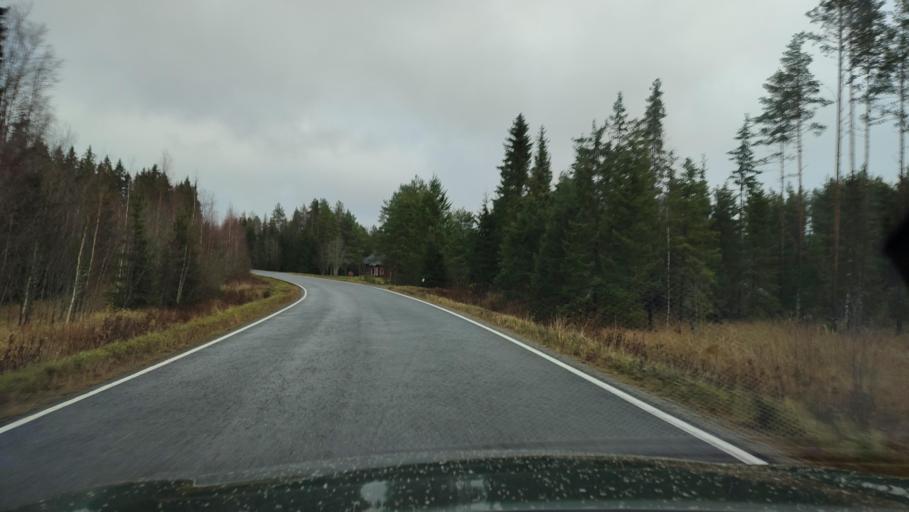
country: FI
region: Ostrobothnia
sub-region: Sydosterbotten
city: Kristinestad
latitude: 62.3421
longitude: 21.5250
